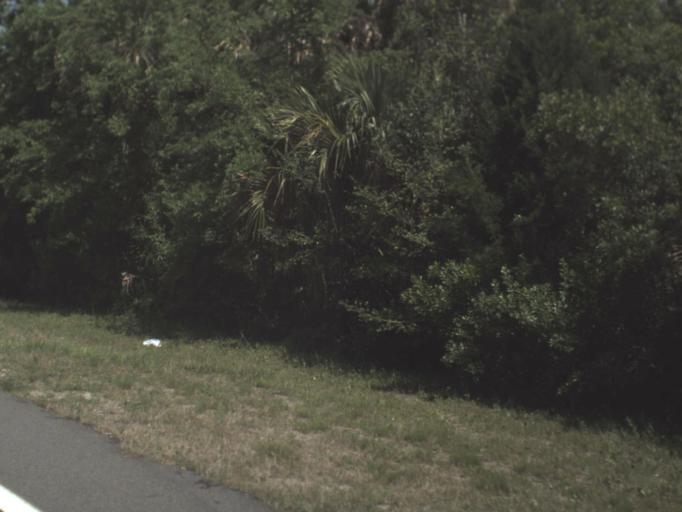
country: US
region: Florida
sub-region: Duval County
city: Atlantic Beach
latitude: 30.3986
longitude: -81.4933
